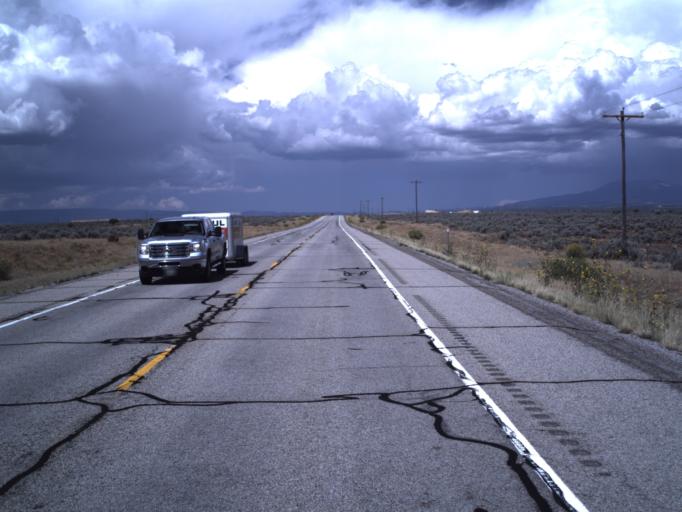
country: US
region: Utah
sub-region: San Juan County
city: Blanding
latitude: 37.5048
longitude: -109.4882
